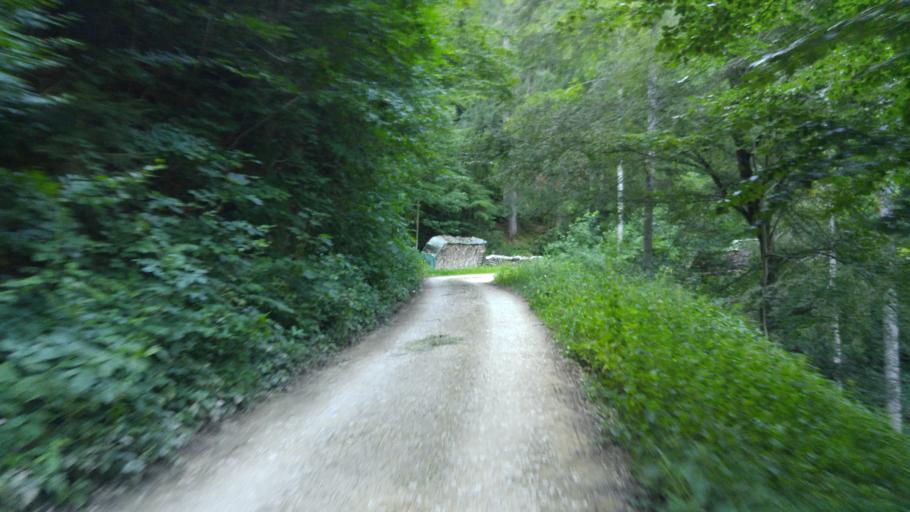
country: DE
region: Baden-Wuerttemberg
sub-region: Freiburg Region
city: Muenstertal/Schwarzwald
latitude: 47.8409
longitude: 7.7909
